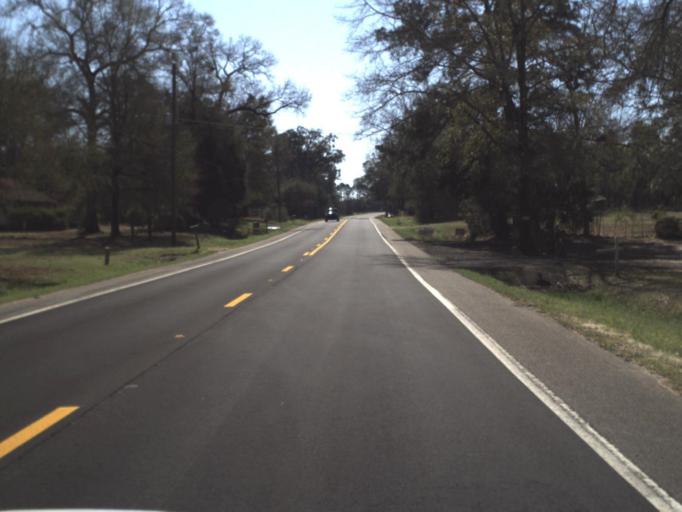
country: US
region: Florida
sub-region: Jackson County
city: Marianna
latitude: 30.6242
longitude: -85.1526
